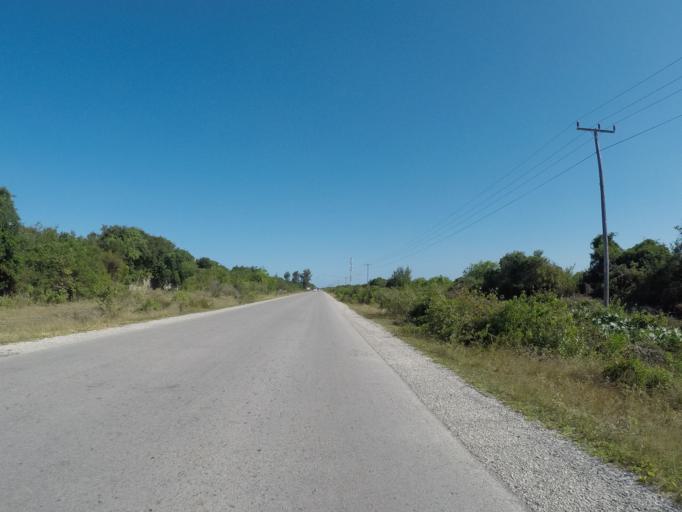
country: TZ
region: Zanzibar Central/South
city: Nganane
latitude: -6.1733
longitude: 39.5266
